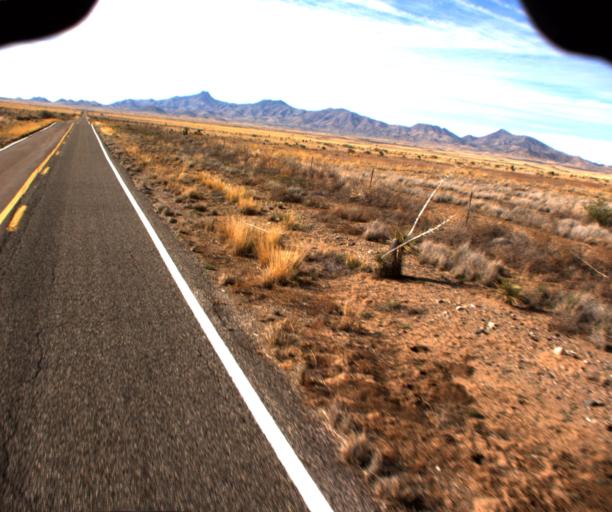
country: US
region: Arizona
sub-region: Cochise County
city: Willcox
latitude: 32.0623
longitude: -109.5031
